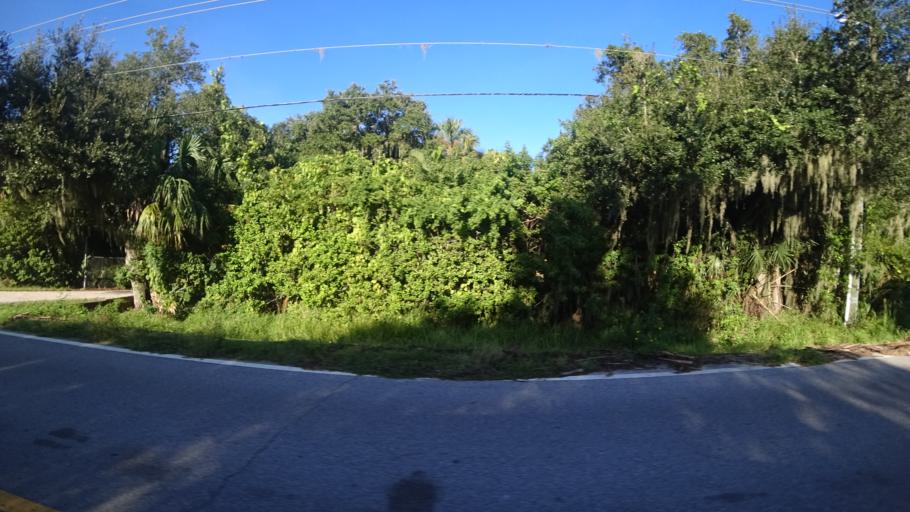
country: US
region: Florida
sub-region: Manatee County
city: Memphis
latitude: 27.5724
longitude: -82.5563
